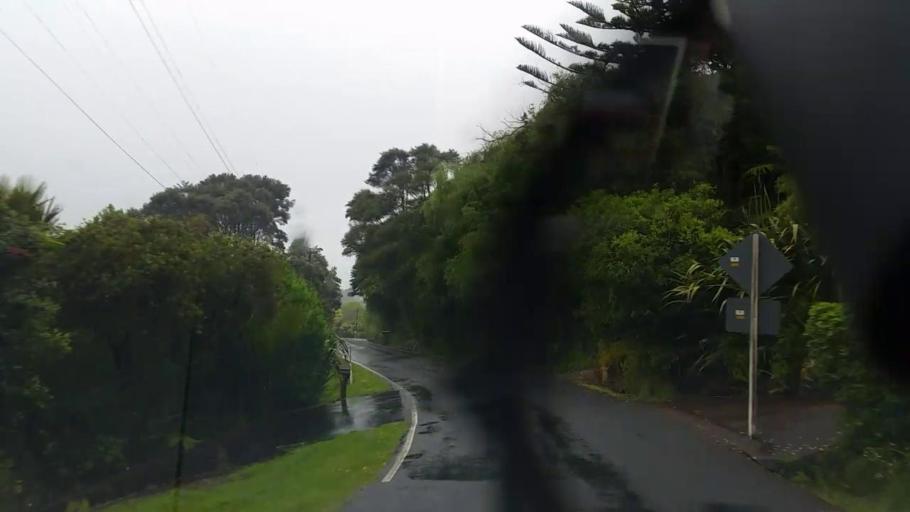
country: NZ
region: Auckland
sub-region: Auckland
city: Waitakere
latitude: -36.9030
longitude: 174.5746
